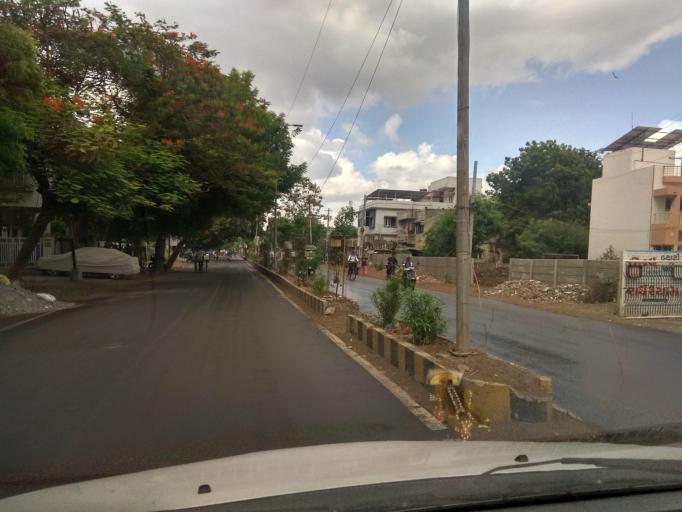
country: IN
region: Gujarat
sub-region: Bhavnagar
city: Bhavnagar
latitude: 21.7597
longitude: 72.1633
